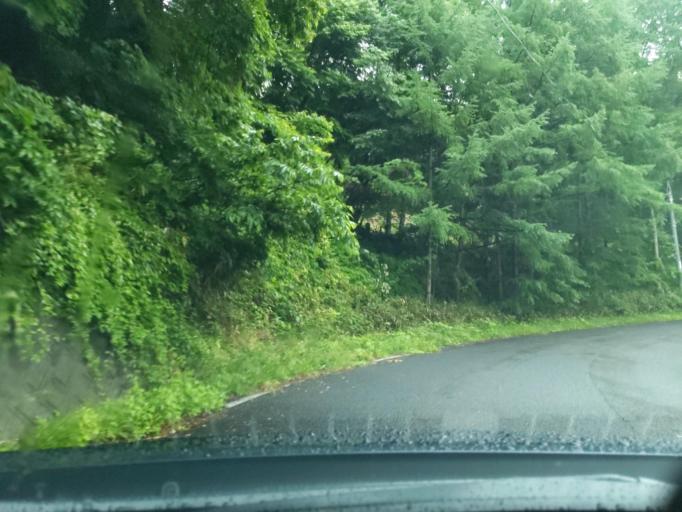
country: JP
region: Fukushima
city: Nihommatsu
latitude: 37.6027
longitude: 140.5708
